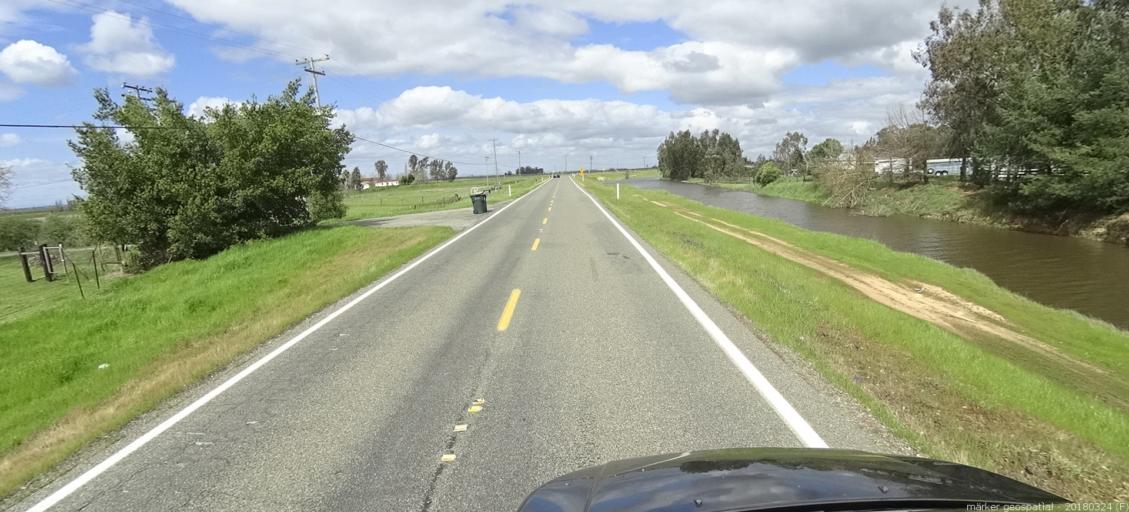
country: US
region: California
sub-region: Sacramento County
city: Elverta
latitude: 38.7100
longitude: -121.4871
